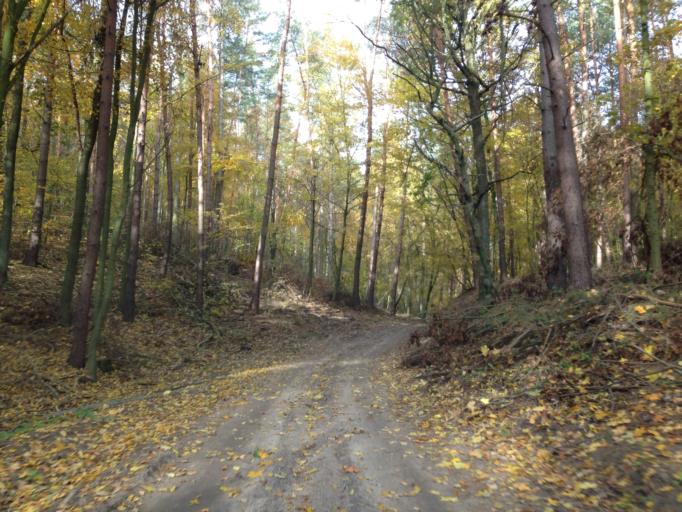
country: PL
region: Kujawsko-Pomorskie
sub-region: Powiat brodnicki
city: Gorzno
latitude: 53.2160
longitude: 19.6516
